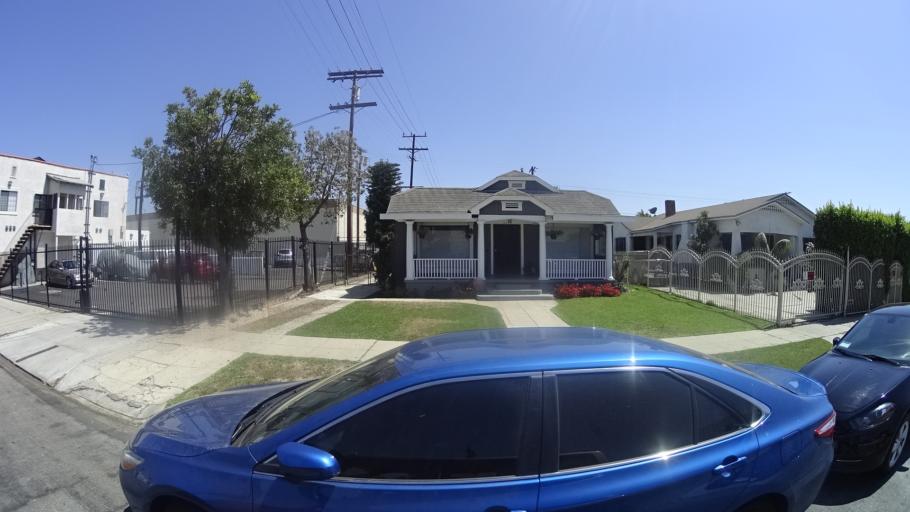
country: US
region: California
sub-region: Los Angeles County
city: View Park-Windsor Hills
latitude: 34.0055
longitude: -118.3094
